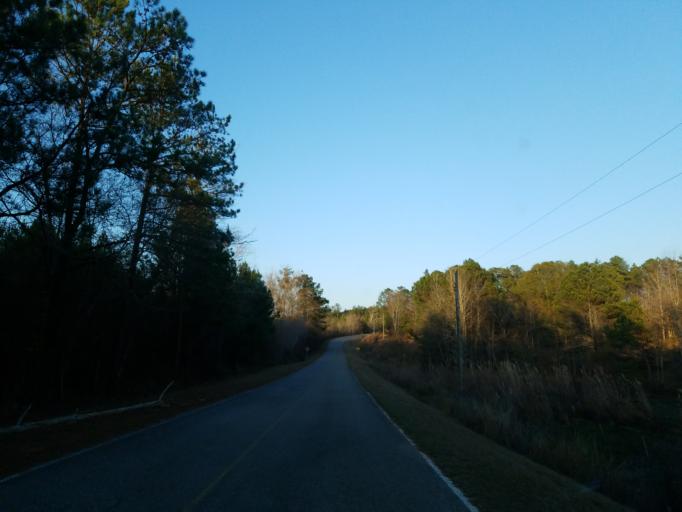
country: US
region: Mississippi
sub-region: Lauderdale County
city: Meridian
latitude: 32.2658
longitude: -88.7800
